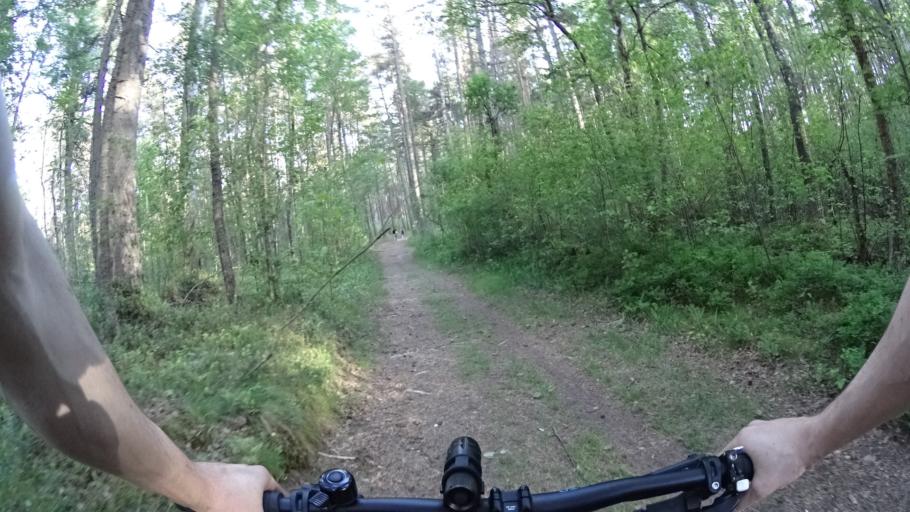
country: LV
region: Riga
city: Jaunciems
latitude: 57.0897
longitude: 24.1383
